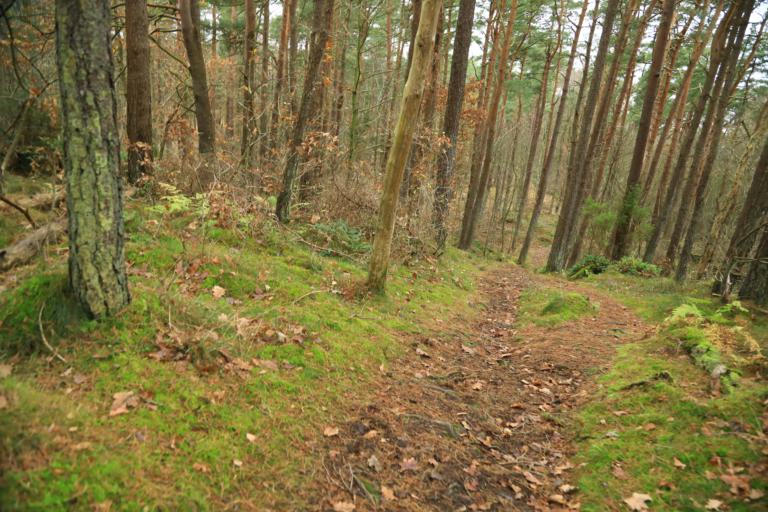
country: SE
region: Halland
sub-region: Varbergs Kommun
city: Varberg
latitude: 57.1780
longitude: 12.2168
